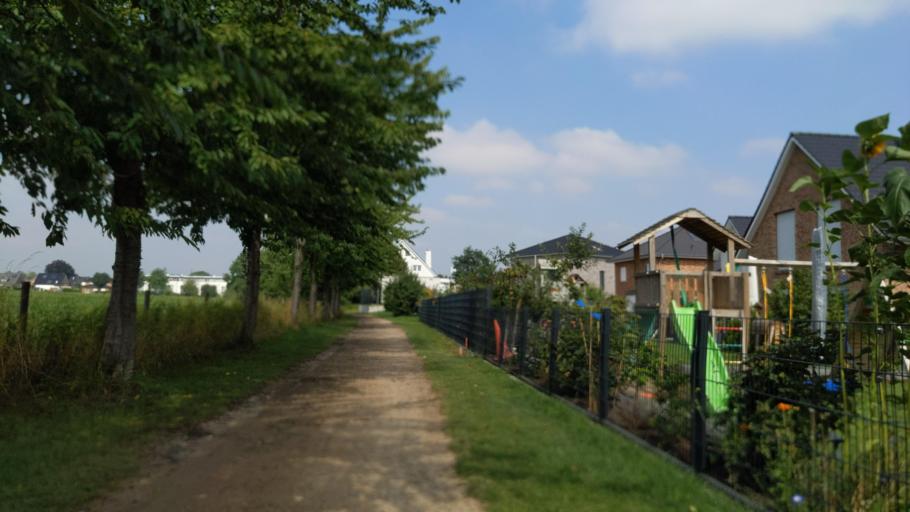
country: DE
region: Schleswig-Holstein
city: Stockelsdorf
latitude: 53.8880
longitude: 10.6333
